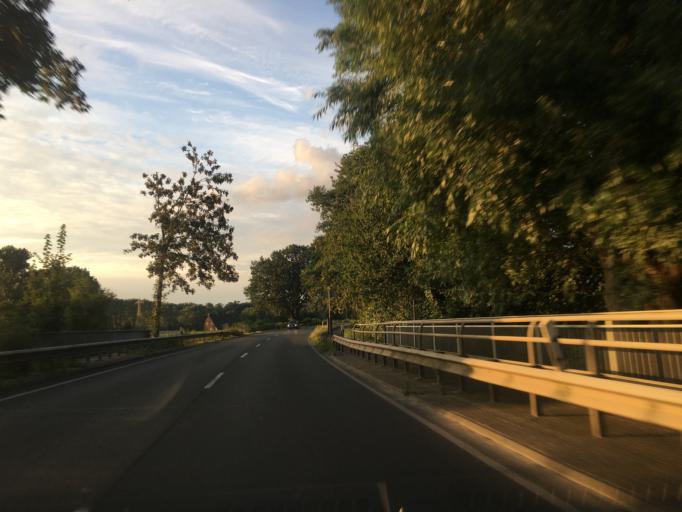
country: DE
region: North Rhine-Westphalia
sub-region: Regierungsbezirk Koln
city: Linnich
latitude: 51.0016
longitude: 6.2764
